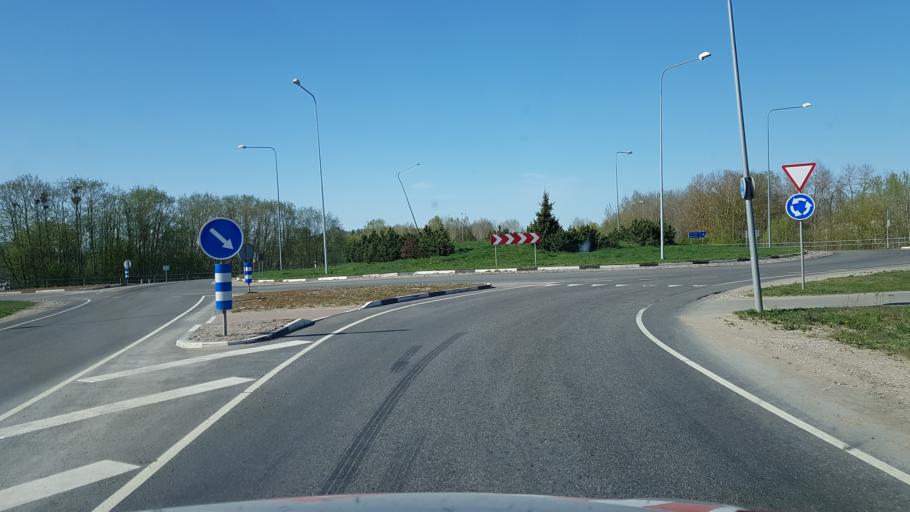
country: EE
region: Viljandimaa
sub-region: Viljandi linn
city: Viljandi
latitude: 58.3550
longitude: 25.5593
